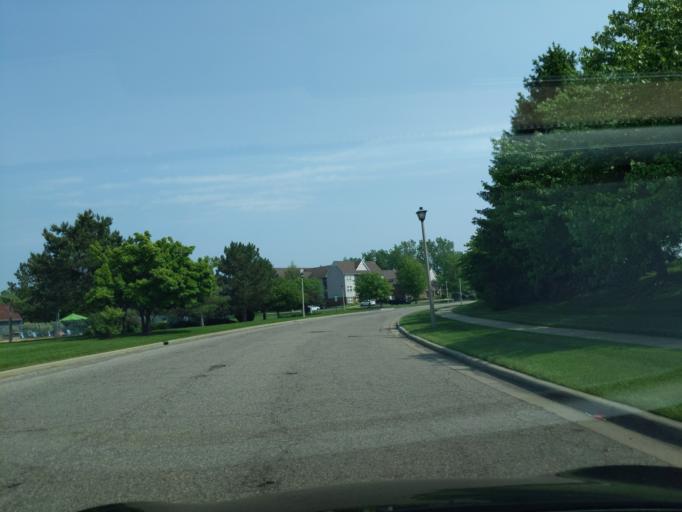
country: US
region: Michigan
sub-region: Eaton County
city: Waverly
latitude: 42.7454
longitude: -84.6568
